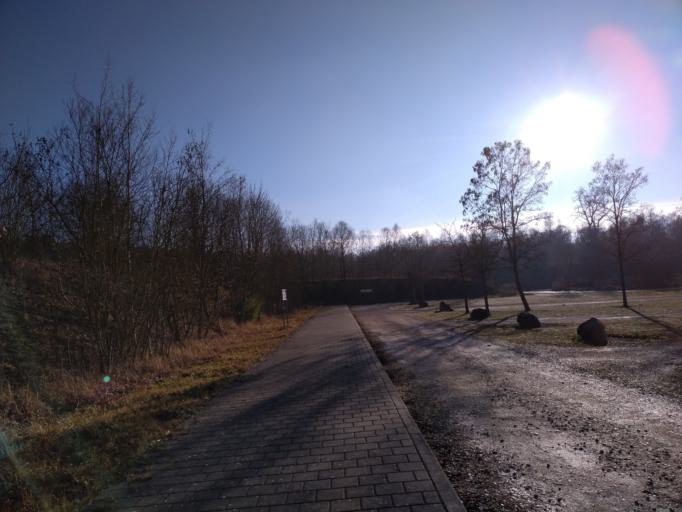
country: DE
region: Bavaria
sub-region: Swabia
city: Wasserburg
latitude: 48.4219
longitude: 10.3001
